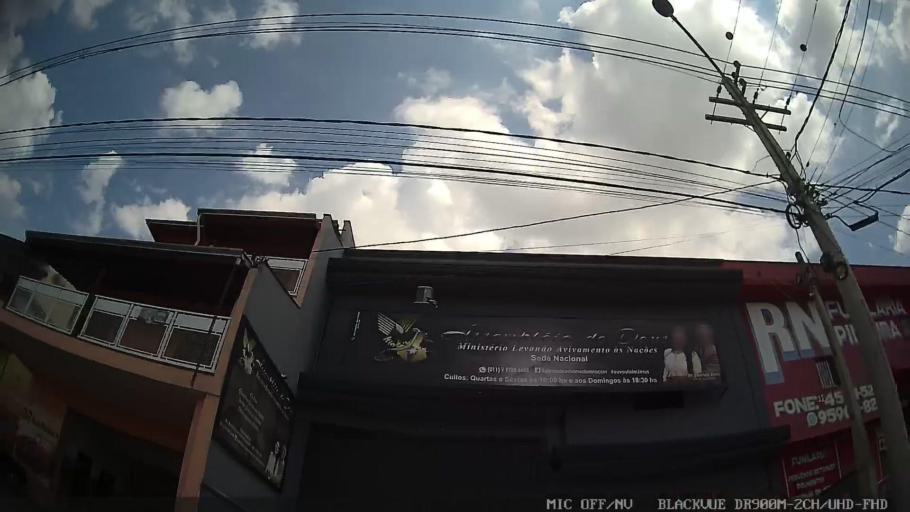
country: BR
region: Sao Paulo
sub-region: Itatiba
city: Itatiba
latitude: -23.0140
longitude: -46.8120
